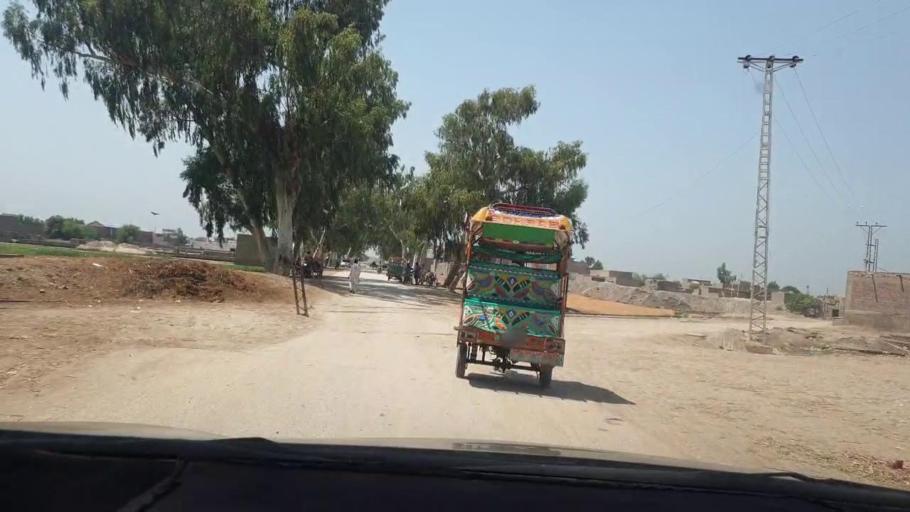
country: PK
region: Sindh
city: Kambar
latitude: 27.5932
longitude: 68.0139
